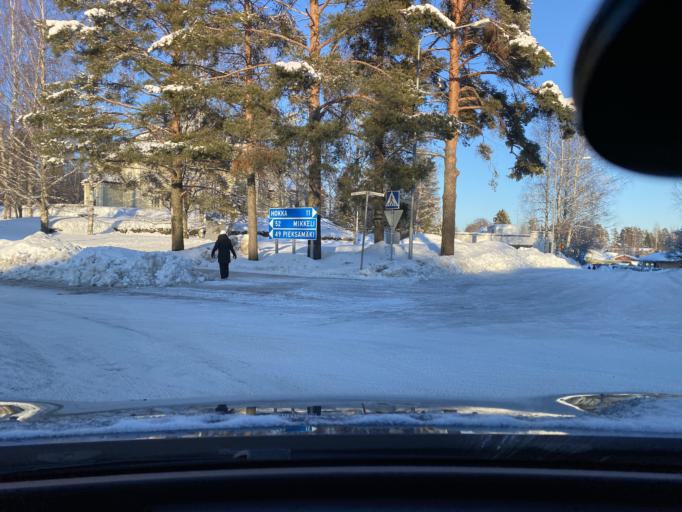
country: FI
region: Southern Savonia
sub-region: Mikkeli
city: Kangasniemi
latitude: 61.9902
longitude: 26.6435
